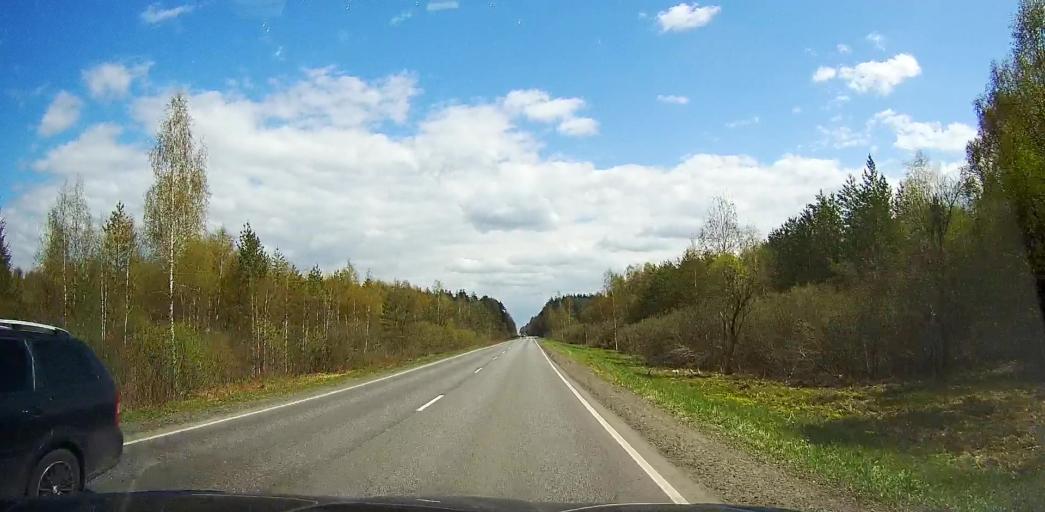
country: RU
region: Moskovskaya
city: Imeni Tsyurupy
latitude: 55.5514
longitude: 38.7172
